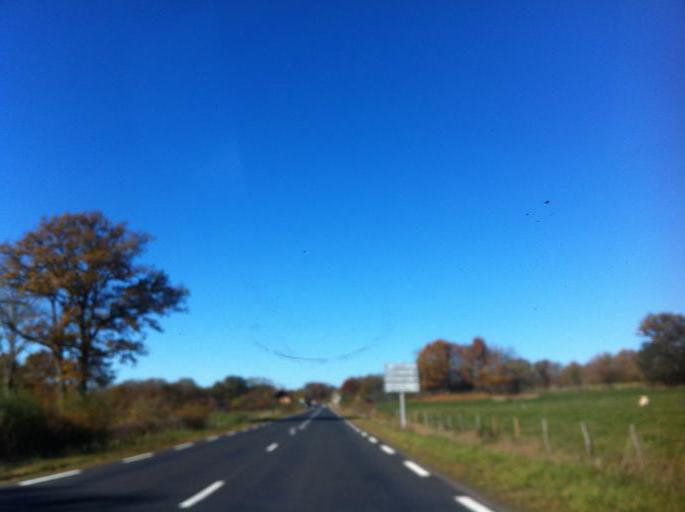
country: FR
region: Auvergne
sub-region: Departement du Puy-de-Dome
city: Gelles
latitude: 45.8594
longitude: 2.6445
